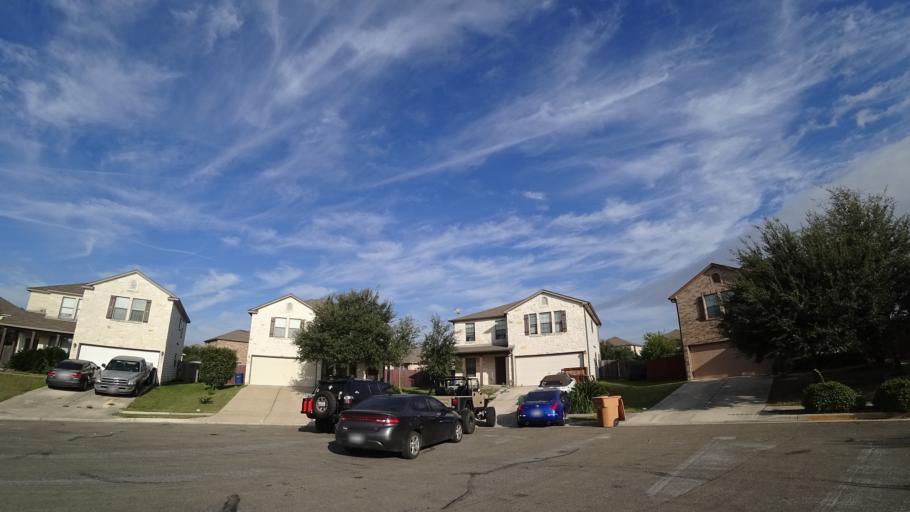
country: US
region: Texas
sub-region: Travis County
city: Austin
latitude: 30.1969
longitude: -97.7279
